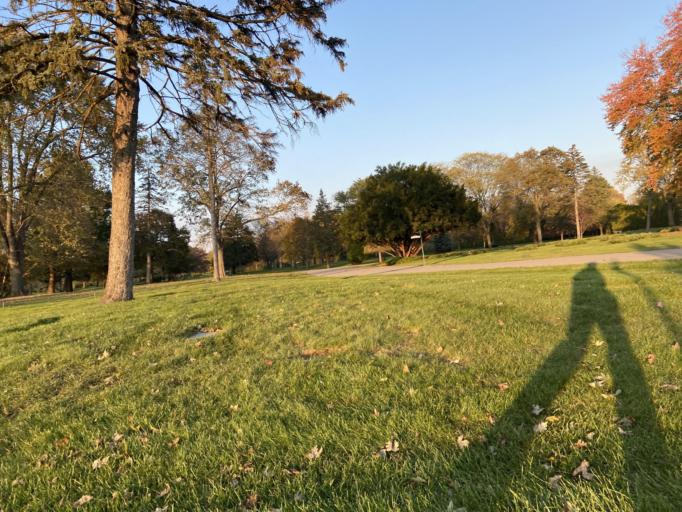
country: US
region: Michigan
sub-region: Wayne County
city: Redford
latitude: 42.4143
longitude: -83.3276
